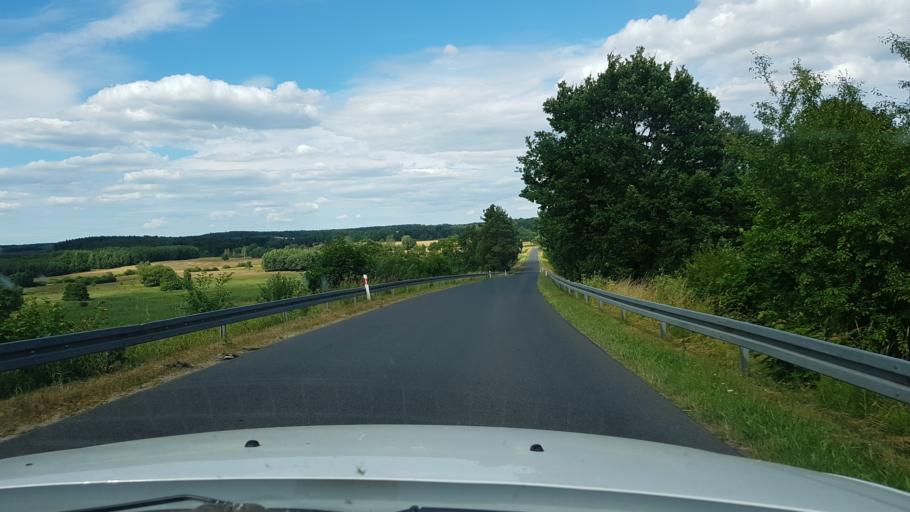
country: PL
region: West Pomeranian Voivodeship
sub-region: Powiat drawski
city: Kalisz Pomorski
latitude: 53.3951
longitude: 15.9595
